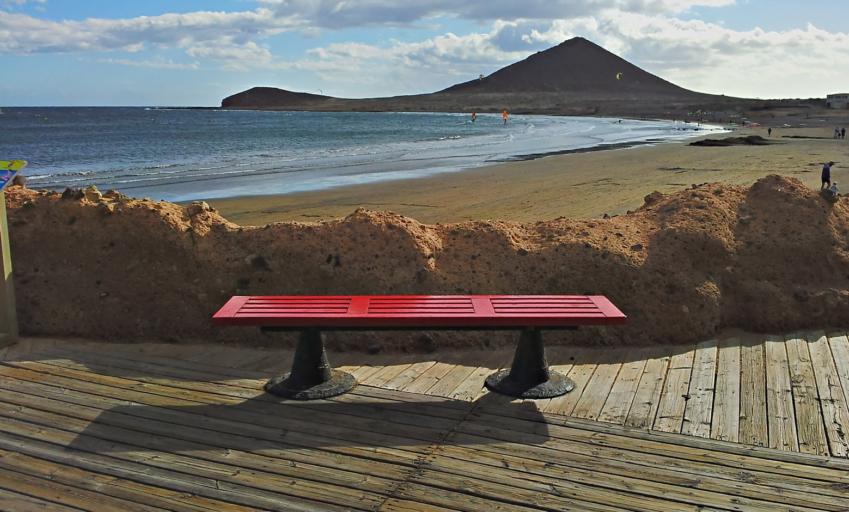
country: ES
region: Canary Islands
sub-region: Provincia de Santa Cruz de Tenerife
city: San Isidro
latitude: 28.0437
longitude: -16.5395
